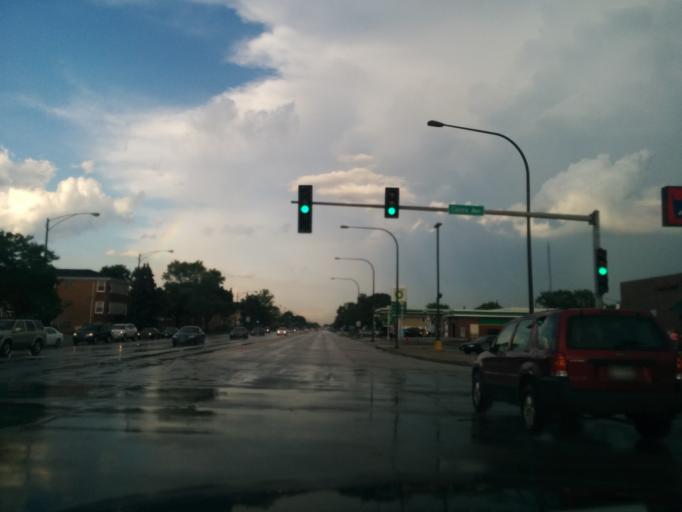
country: US
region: Illinois
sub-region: Cook County
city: Hometown
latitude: 41.7345
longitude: -87.7412
